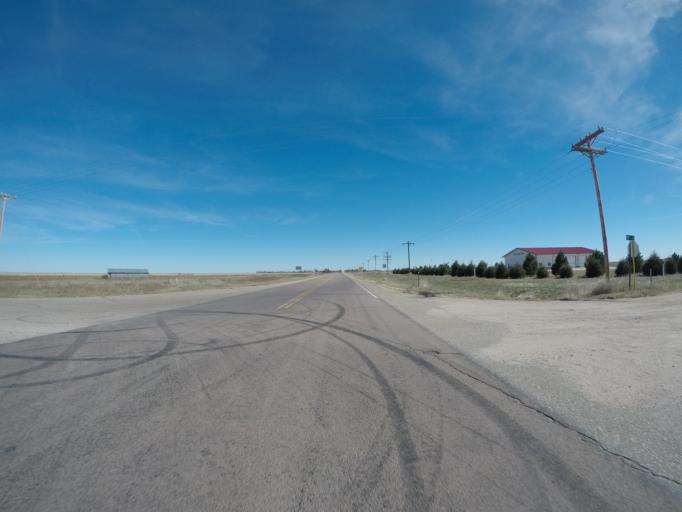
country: US
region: Colorado
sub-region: Yuma County
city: Yuma
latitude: 39.6559
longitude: -102.7072
